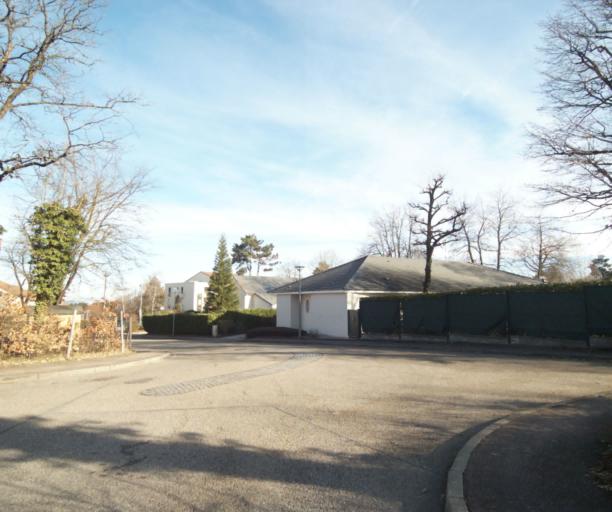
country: FR
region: Lorraine
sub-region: Departement de Meurthe-et-Moselle
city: Villers-les-Nancy
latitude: 48.6487
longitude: 6.1563
